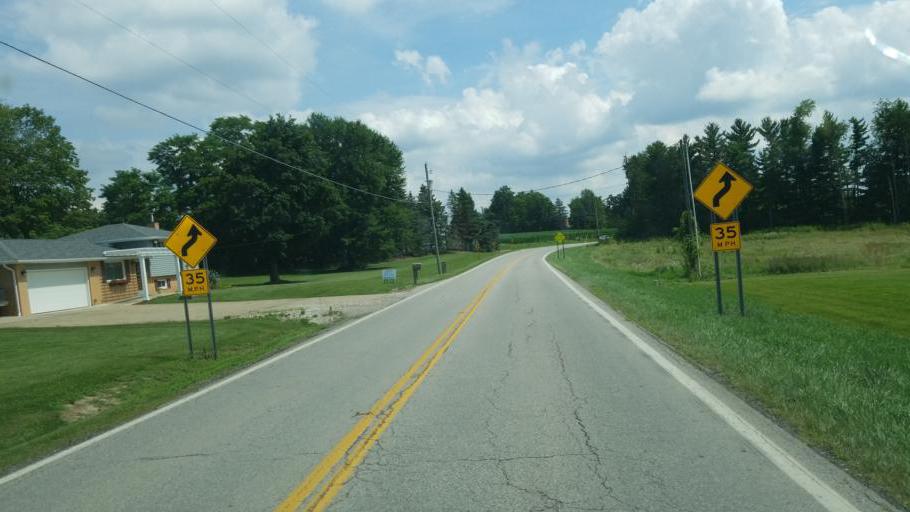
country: US
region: Ohio
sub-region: Richland County
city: Lexington
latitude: 40.6679
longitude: -82.5603
